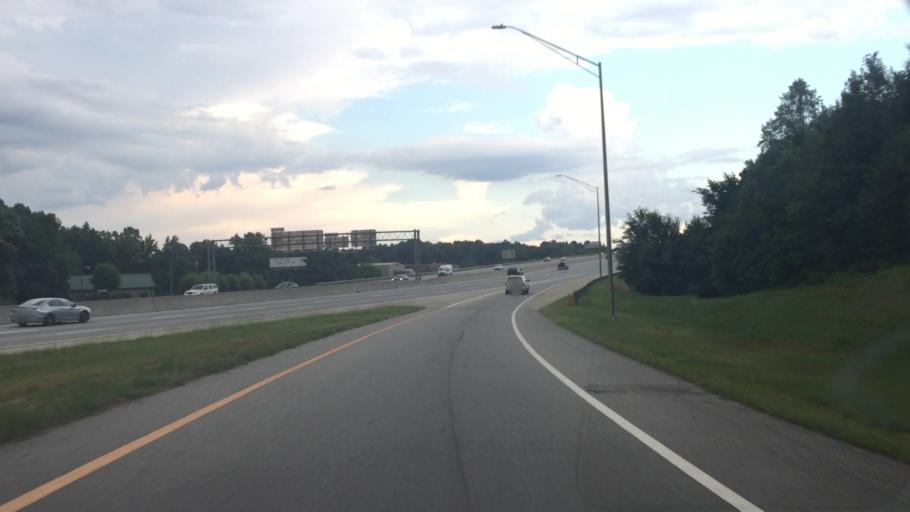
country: US
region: North Carolina
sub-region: Rowan County
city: Salisbury
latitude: 35.6438
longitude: -80.4785
